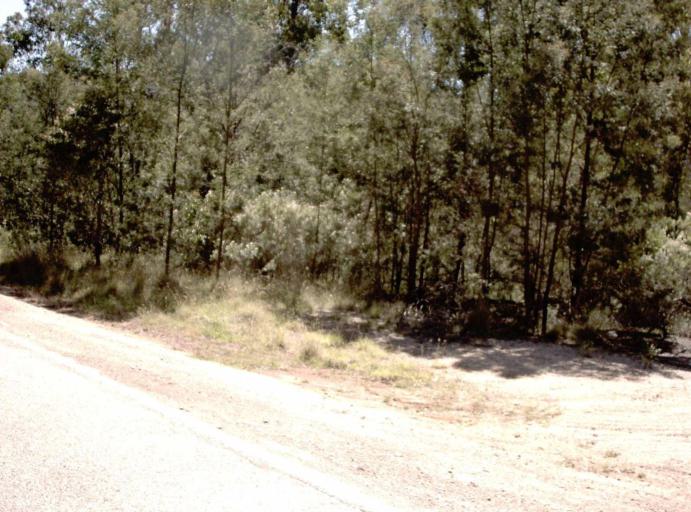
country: AU
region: Victoria
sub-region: East Gippsland
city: Lakes Entrance
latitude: -37.4015
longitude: 148.2144
